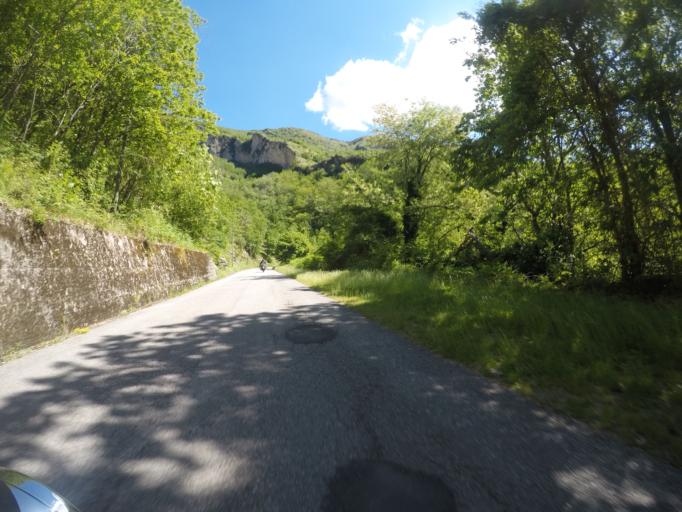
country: IT
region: Tuscany
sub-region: Provincia di Lucca
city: Careggine
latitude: 44.0694
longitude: 10.3096
